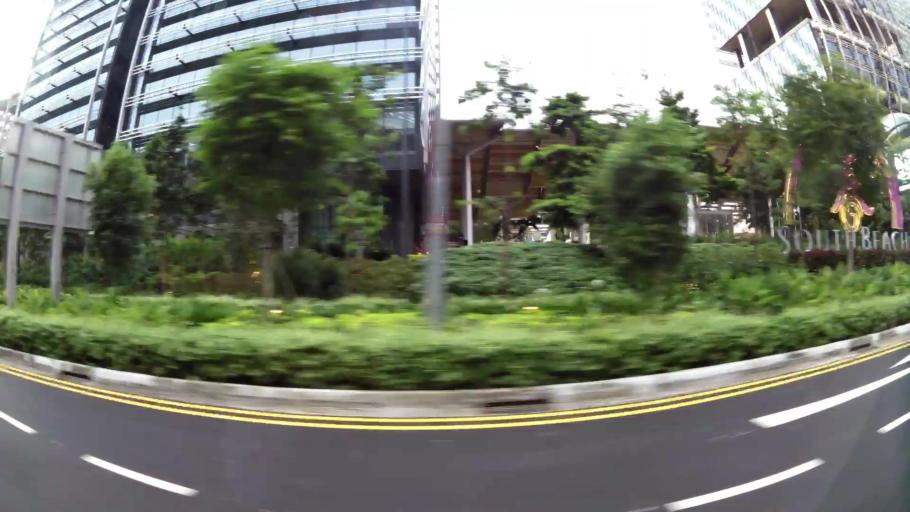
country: SG
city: Singapore
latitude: 1.2942
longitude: 103.8565
